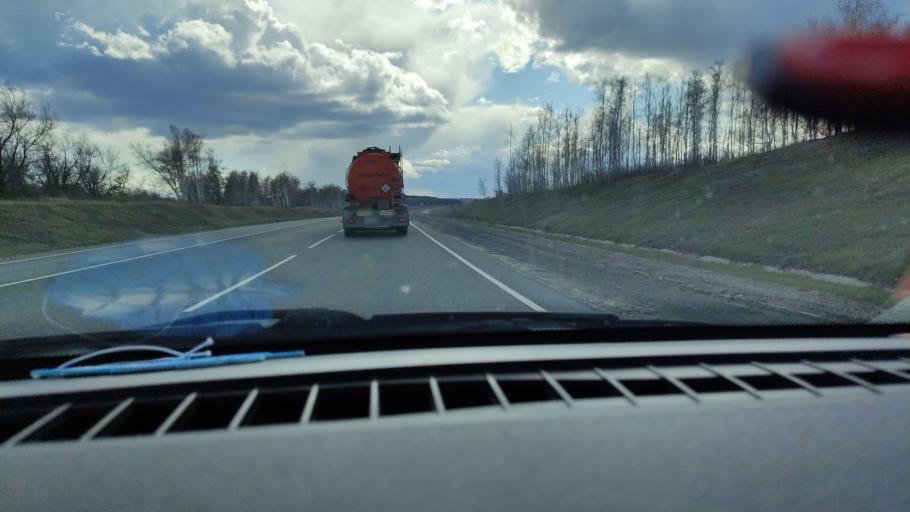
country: RU
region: Saratov
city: Khvalynsk
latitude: 52.5557
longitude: 48.0817
